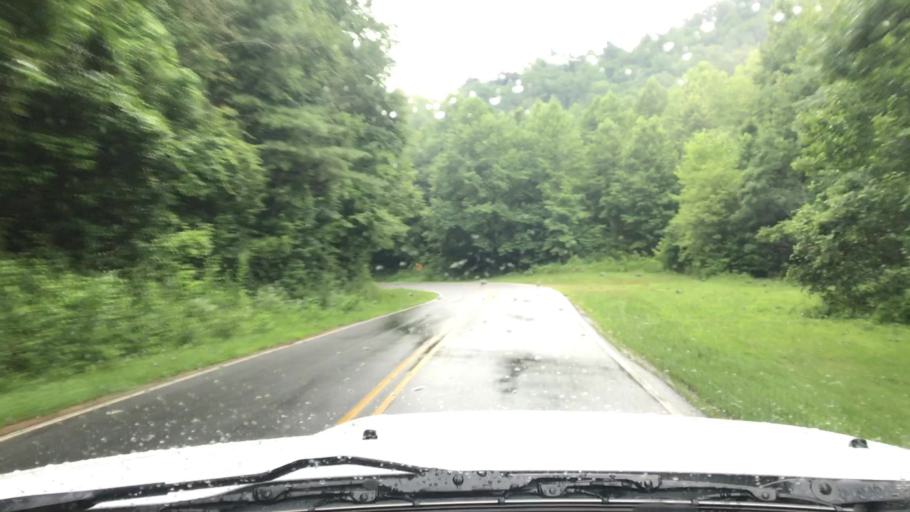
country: US
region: North Carolina
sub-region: Graham County
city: Robbinsville
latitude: 35.3988
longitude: -83.8780
